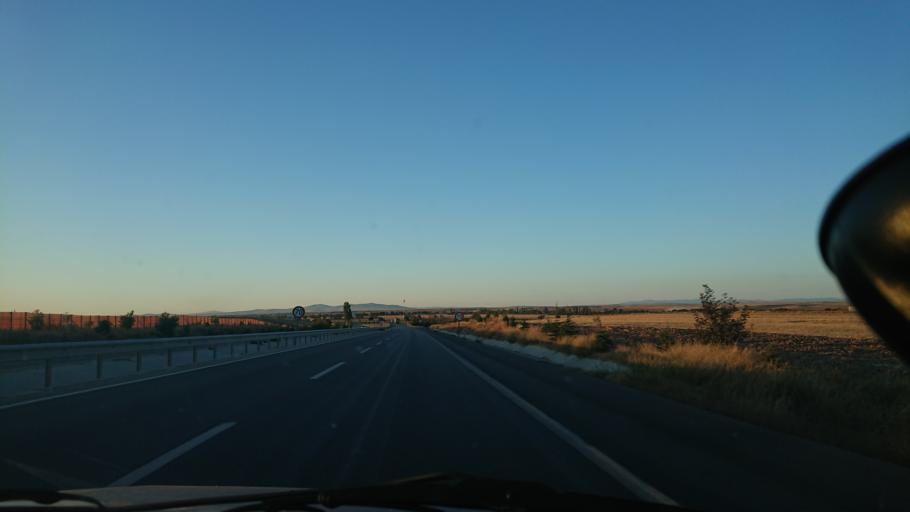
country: TR
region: Eskisehir
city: Mahmudiye
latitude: 39.5132
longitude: 30.9640
